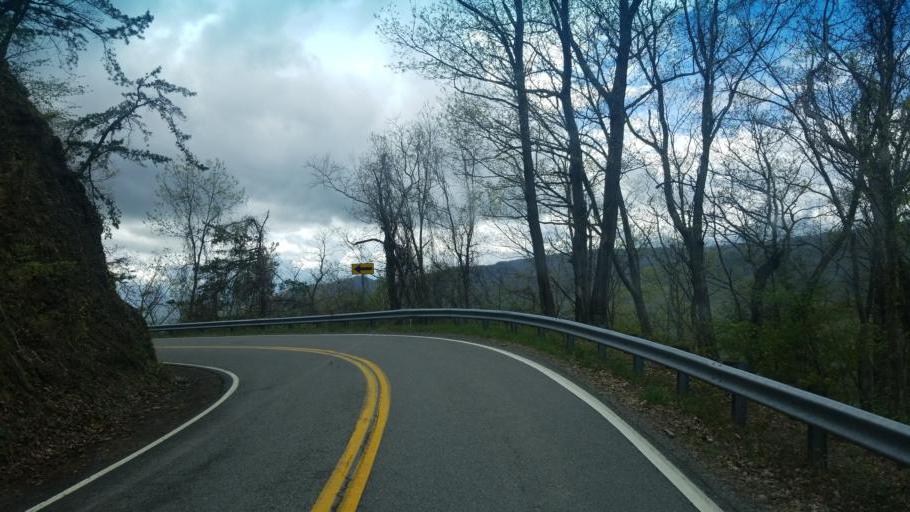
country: US
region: Virginia
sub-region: Tazewell County
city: Tazewell
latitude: 37.0026
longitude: -81.5274
